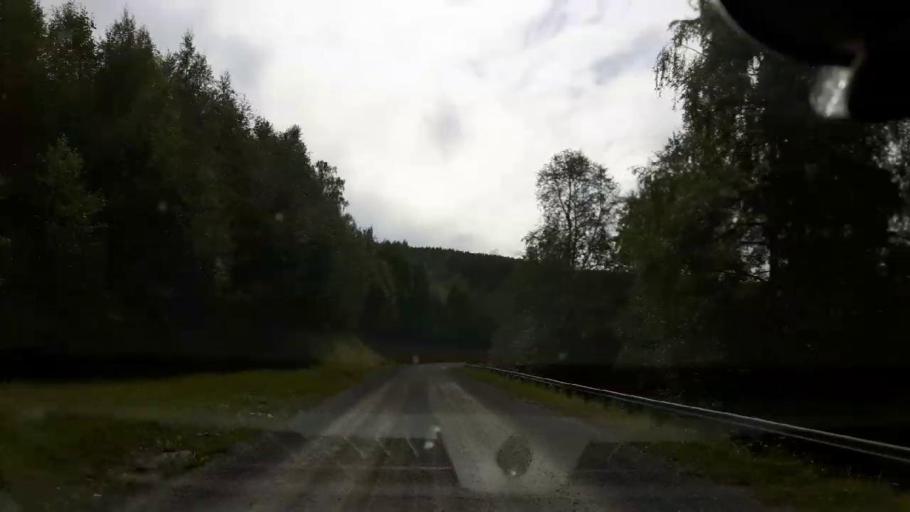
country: SE
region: Jaemtland
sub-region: Ragunda Kommun
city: Hammarstrand
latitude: 63.1332
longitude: 16.0799
